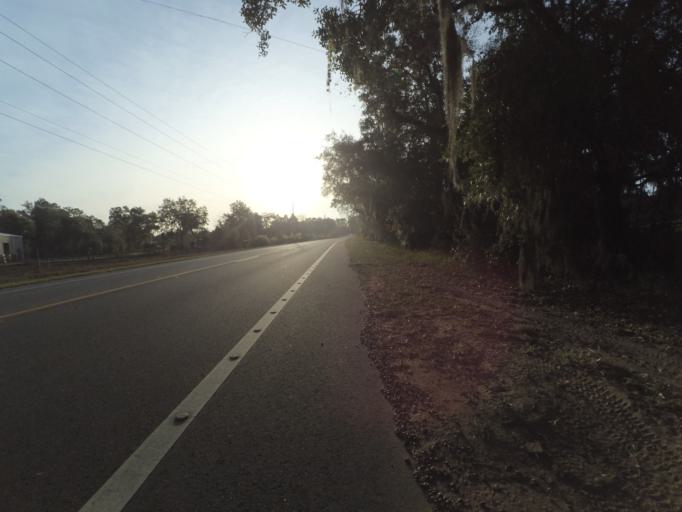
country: US
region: Florida
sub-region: Lake County
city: Umatilla
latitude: 28.9340
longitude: -81.7002
